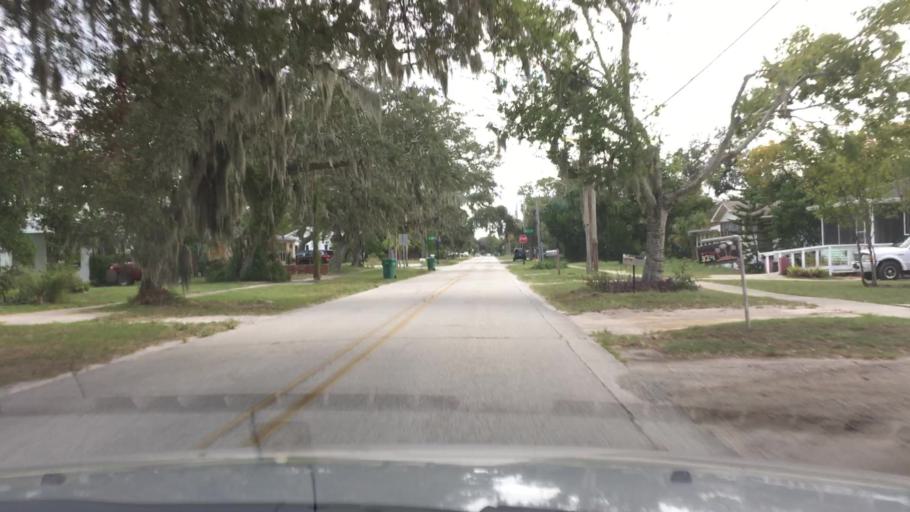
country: US
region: Florida
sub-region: Volusia County
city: Holly Hill
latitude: 29.2330
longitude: -81.0323
